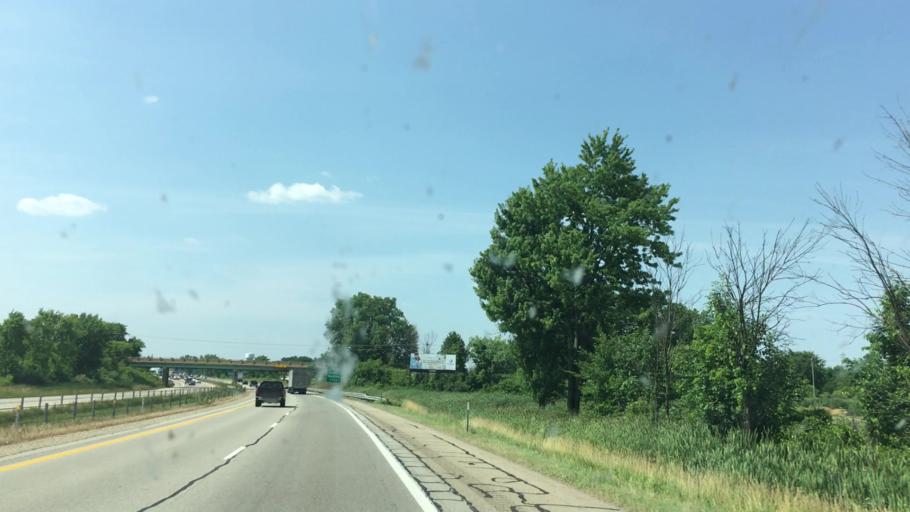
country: US
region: Michigan
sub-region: Allegan County
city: Wayland
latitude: 42.7085
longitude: -85.6603
